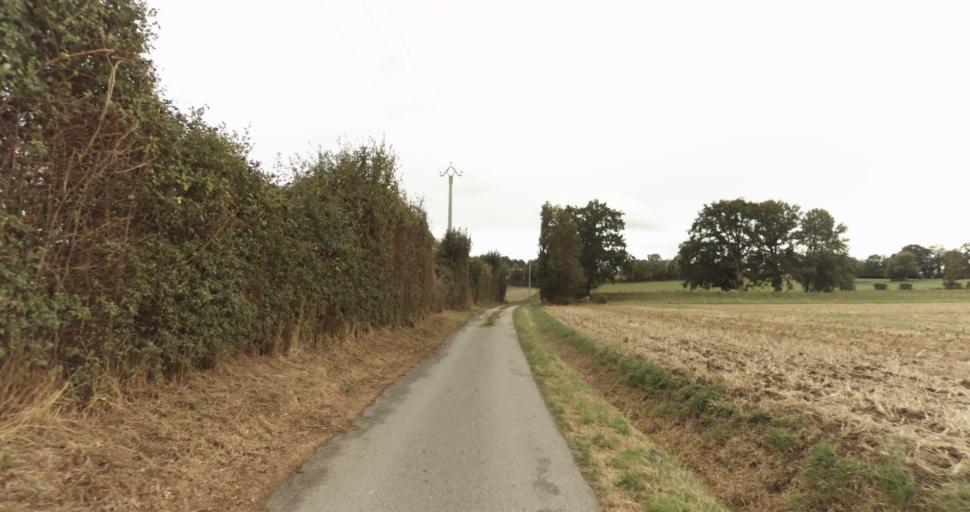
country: FR
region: Lower Normandy
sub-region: Departement de l'Orne
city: Gace
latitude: 48.6938
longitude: 0.2538
